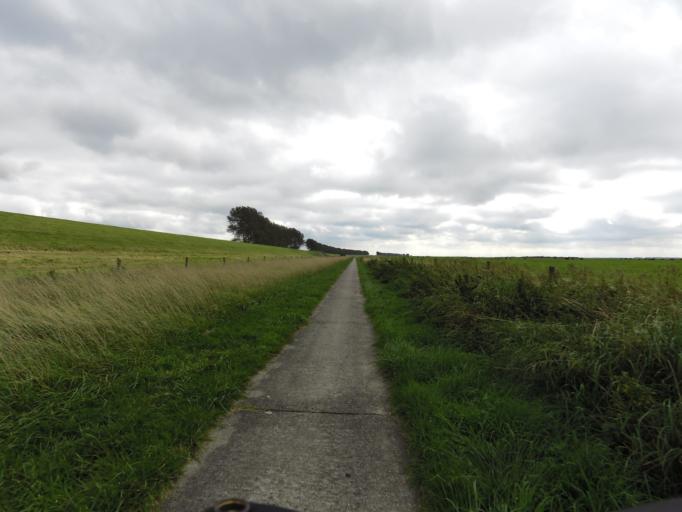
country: NL
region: South Holland
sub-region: Gemeente Goeree-Overflakkee
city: Dirksland
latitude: 51.7527
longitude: 4.0517
